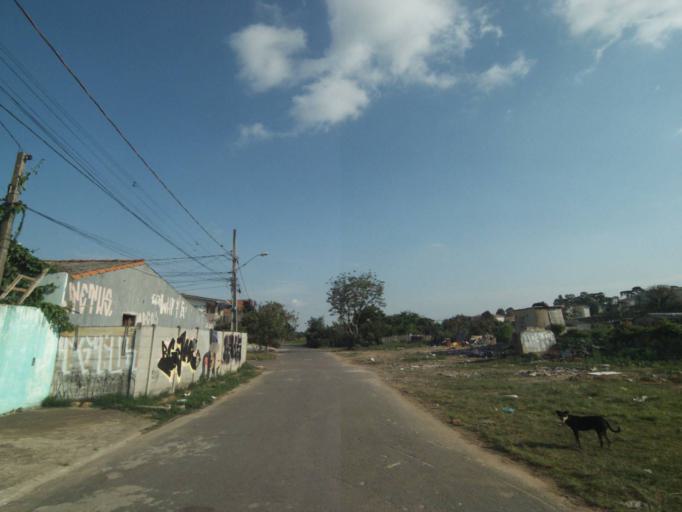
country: BR
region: Parana
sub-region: Curitiba
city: Curitiba
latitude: -25.4852
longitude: -49.3371
